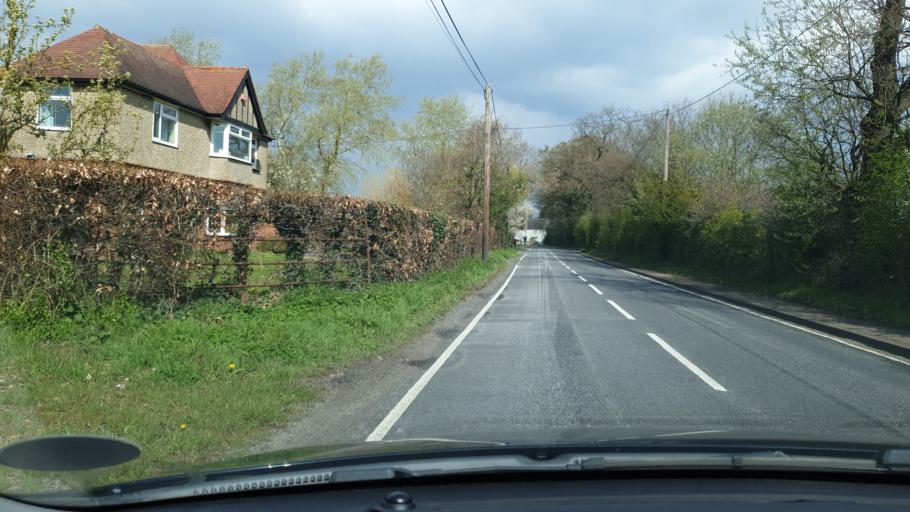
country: GB
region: England
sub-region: Essex
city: Great Bentley
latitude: 51.8877
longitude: 1.1099
